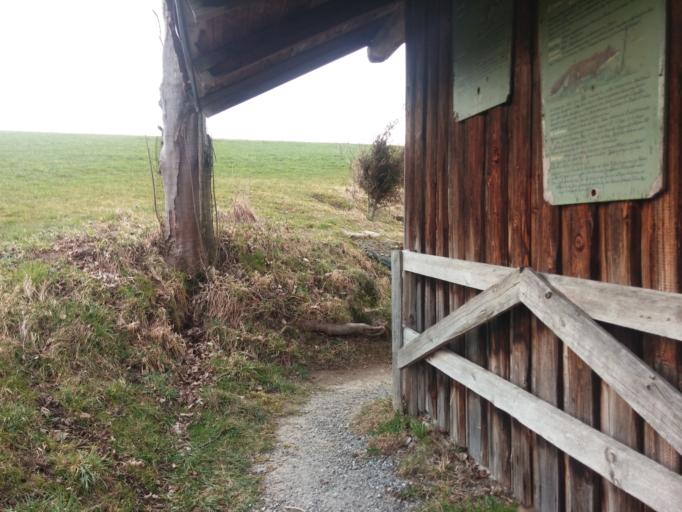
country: DE
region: Bavaria
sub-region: Swabia
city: Wildpoldsried
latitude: 47.7652
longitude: 10.3965
